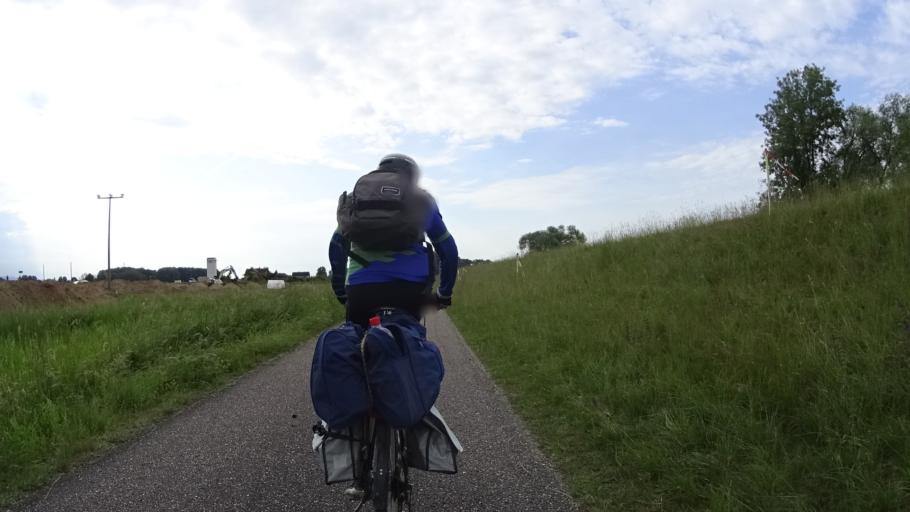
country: DE
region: Bavaria
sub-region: Lower Bavaria
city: Irlbach
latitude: 48.8679
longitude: 12.7597
